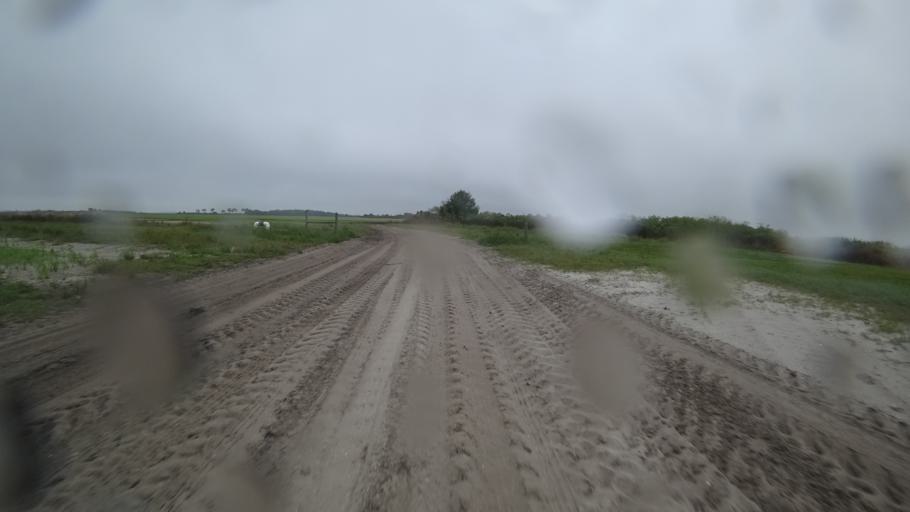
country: US
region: Florida
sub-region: Sarasota County
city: Warm Mineral Springs
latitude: 27.2953
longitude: -82.1609
